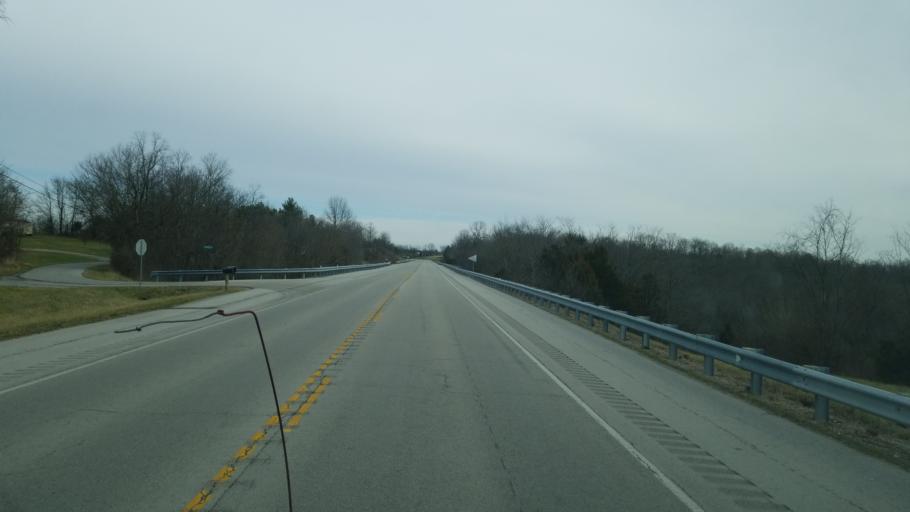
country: US
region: Kentucky
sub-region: Robertson County
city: Mount Olivet
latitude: 38.4538
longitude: -83.9601
